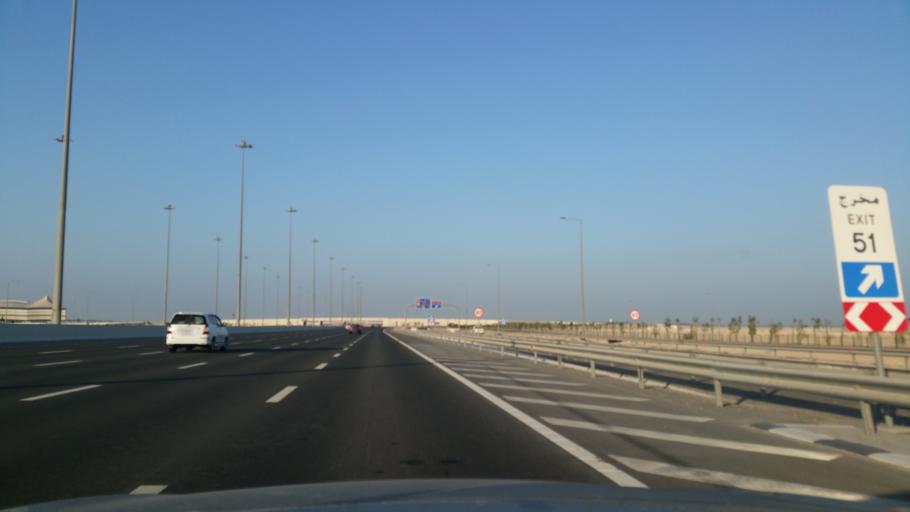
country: QA
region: Baladiyat az Za`ayin
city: Az Za`ayin
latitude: 25.6315
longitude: 51.4892
